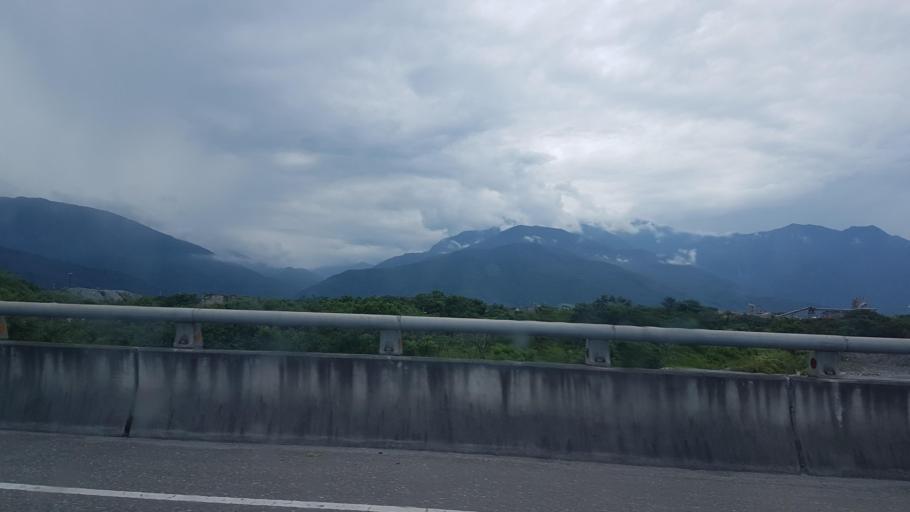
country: TW
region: Taiwan
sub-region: Hualien
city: Hualian
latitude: 23.9208
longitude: 121.5860
